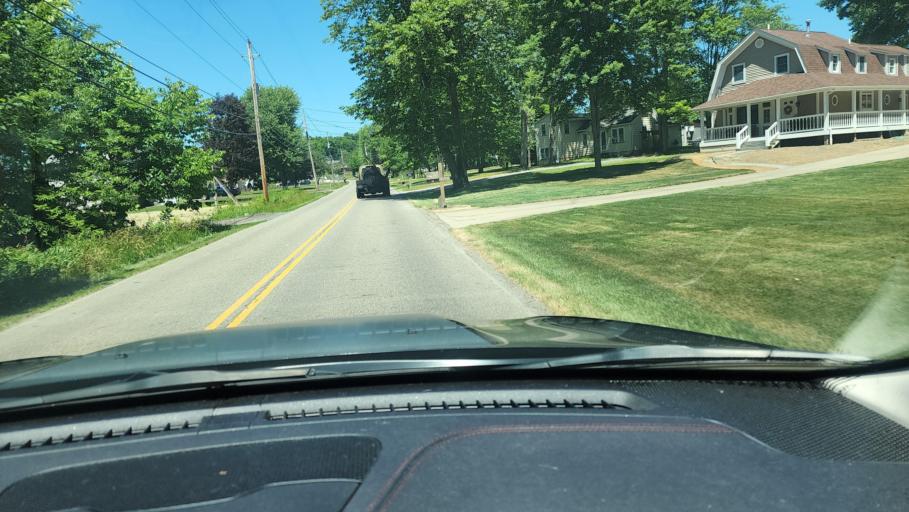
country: US
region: Ohio
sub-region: Mahoning County
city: Austintown
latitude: 41.0763
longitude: -80.7905
